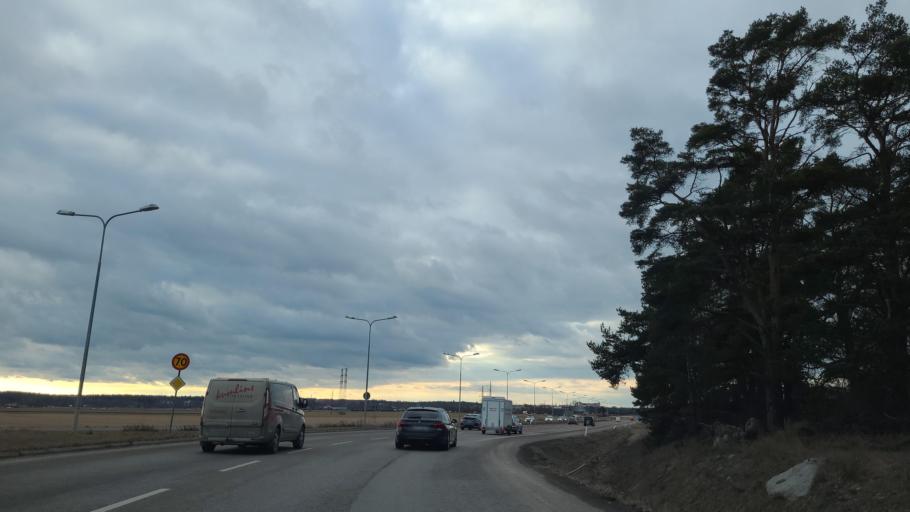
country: SE
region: Uppsala
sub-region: Uppsala Kommun
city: Saevja
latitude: 59.8397
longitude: 17.7017
